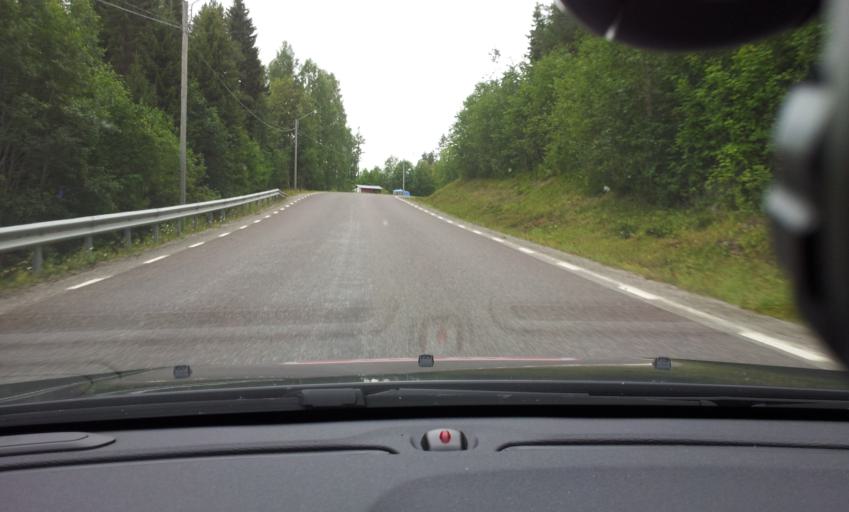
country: SE
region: Jaemtland
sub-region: Braecke Kommun
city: Braecke
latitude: 63.0430
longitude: 15.2870
